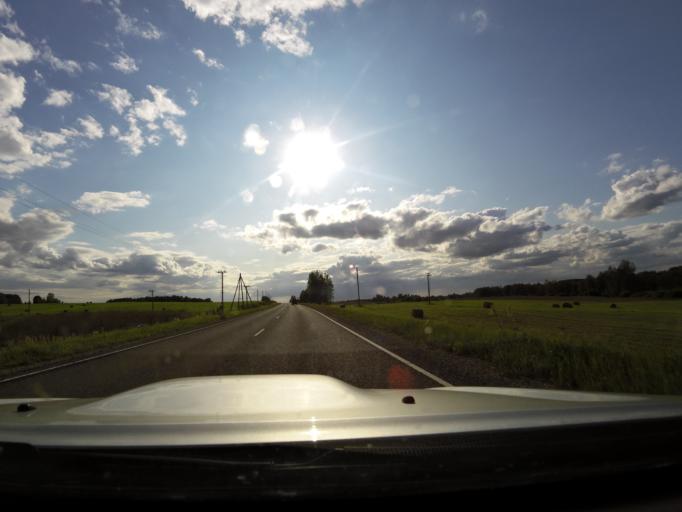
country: LV
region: Viesite
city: Viesite
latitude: 56.1989
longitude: 25.5011
